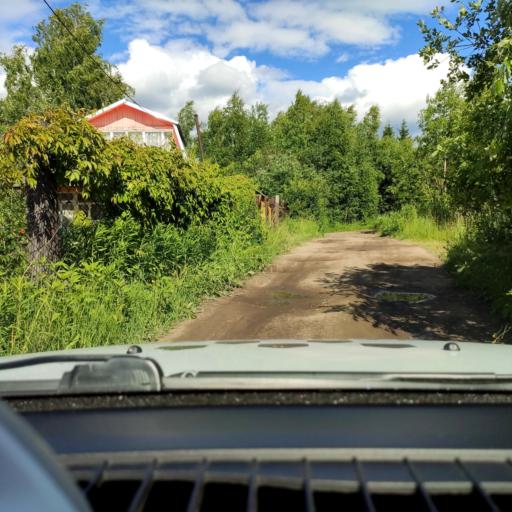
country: RU
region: Perm
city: Overyata
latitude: 58.1034
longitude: 55.8677
